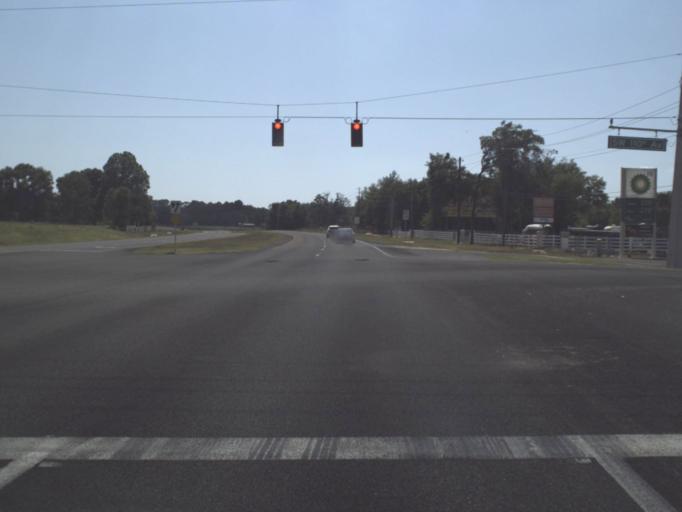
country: US
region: Florida
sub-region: Marion County
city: Ocala
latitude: 29.1869
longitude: -82.3016
